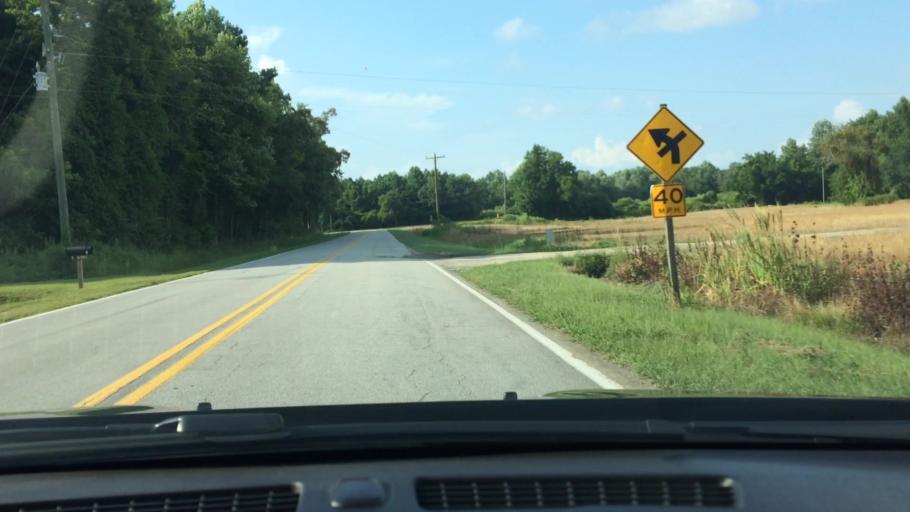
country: US
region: North Carolina
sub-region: Beaufort County
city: River Road
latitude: 35.4559
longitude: -77.0208
